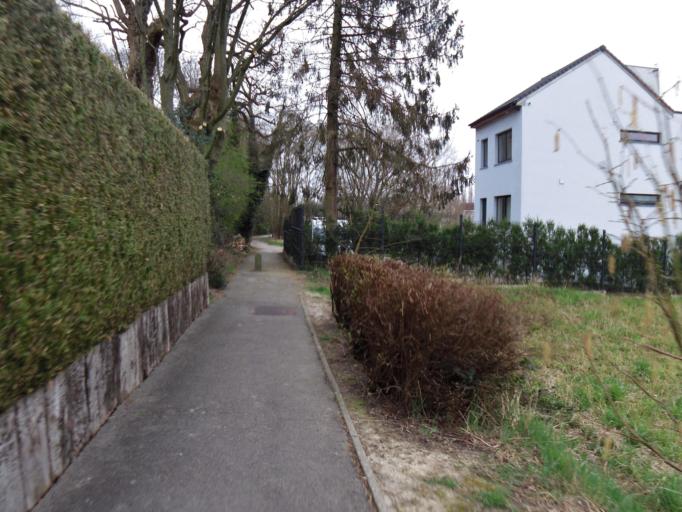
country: BE
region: Flanders
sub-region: Provincie Vlaams-Brabant
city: Dilbeek
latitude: 50.8407
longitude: 4.2728
